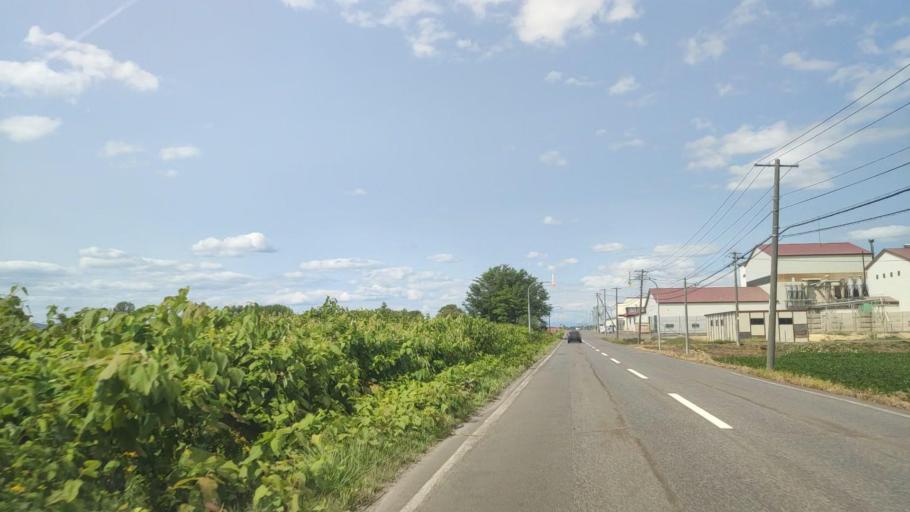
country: JP
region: Hokkaido
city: Nayoro
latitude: 44.2027
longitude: 142.4158
